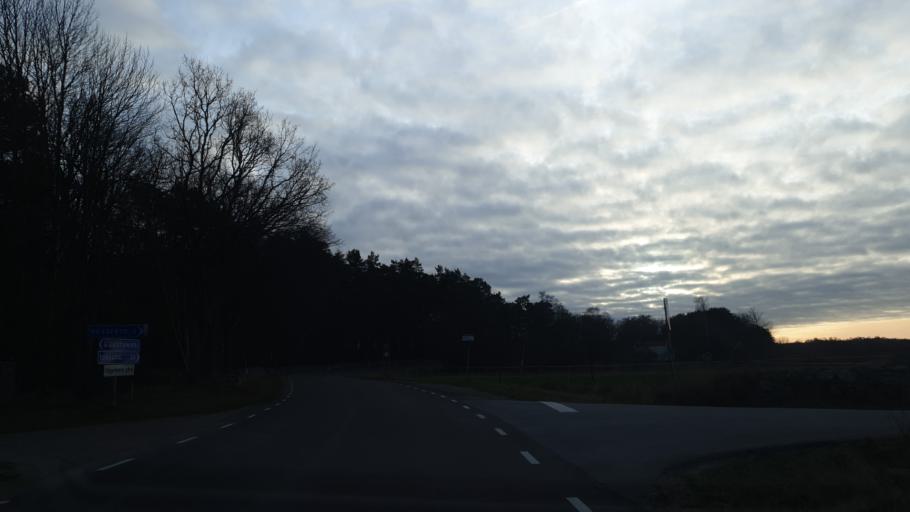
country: SE
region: Kalmar
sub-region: Torsas Kommun
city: Torsas
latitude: 56.2327
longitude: 15.9973
